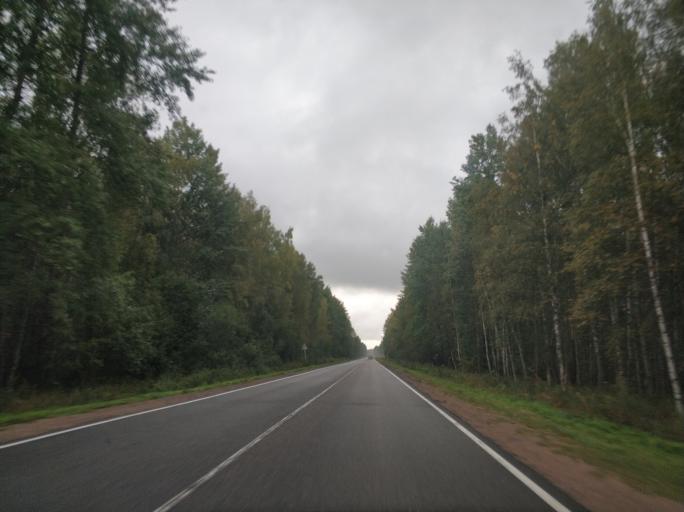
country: RU
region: Leningrad
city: Borisova Griva
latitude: 60.1192
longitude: 30.9636
